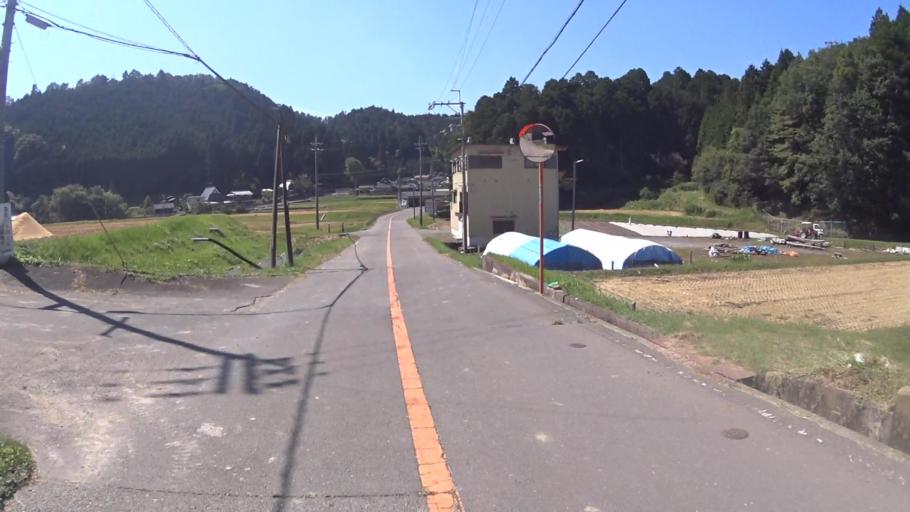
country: JP
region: Kyoto
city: Kameoka
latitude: 34.9611
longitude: 135.6102
